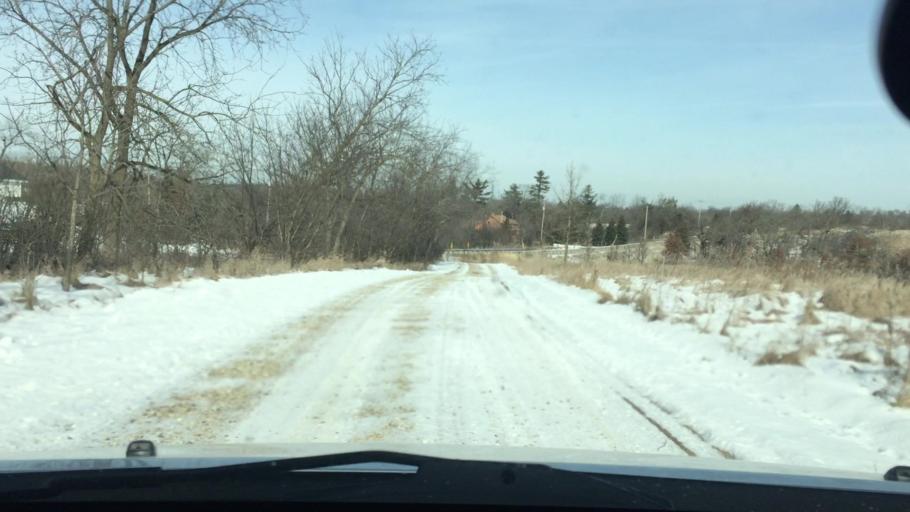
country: US
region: Wisconsin
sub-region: Waukesha County
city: Eagle
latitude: 42.8702
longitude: -88.4832
